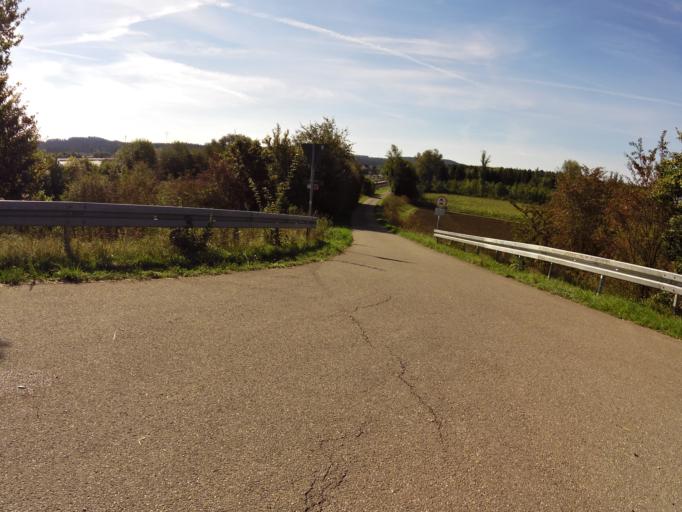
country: DE
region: Baden-Wuerttemberg
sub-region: Freiburg Region
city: Deisslingen
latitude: 48.0915
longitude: 8.5850
